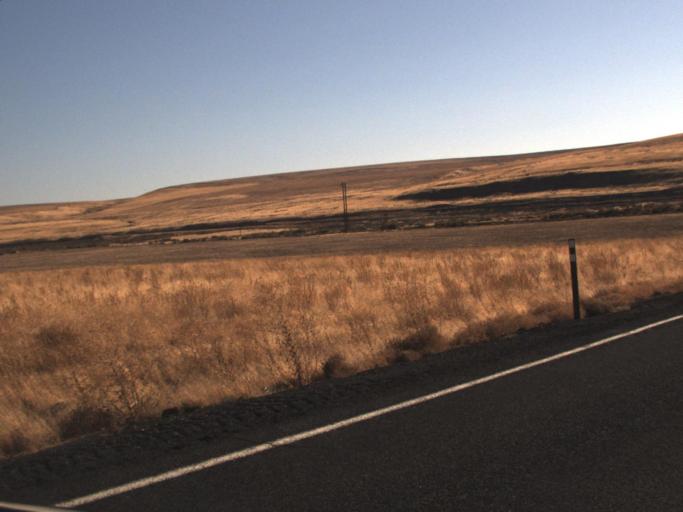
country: US
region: Washington
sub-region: Adams County
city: Ritzville
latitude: 46.9749
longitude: -118.6638
